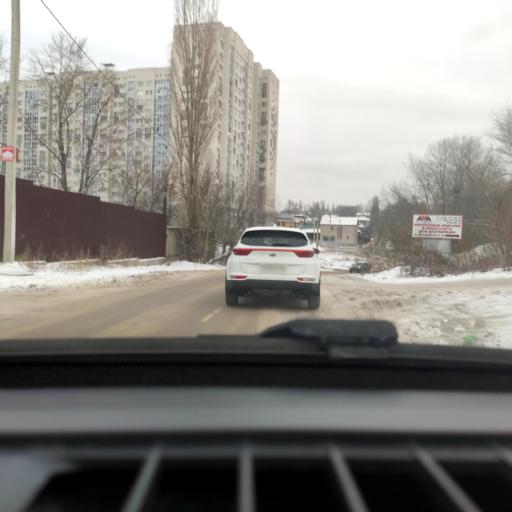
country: RU
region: Voronezj
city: Voronezh
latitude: 51.6713
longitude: 39.1358
